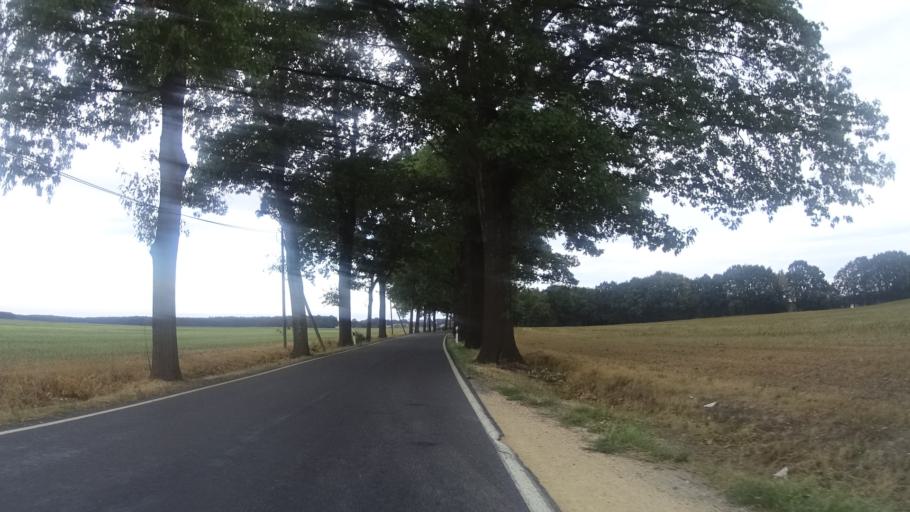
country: DE
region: Saxony
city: Rothenburg
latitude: 51.3025
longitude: 15.0081
